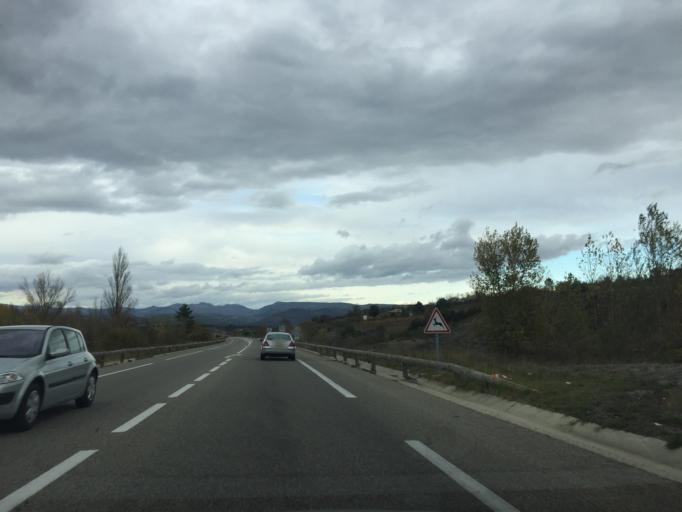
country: FR
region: Rhone-Alpes
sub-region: Departement de l'Ardeche
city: Lachapelle-sous-Aubenas
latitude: 44.5662
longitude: 4.3725
